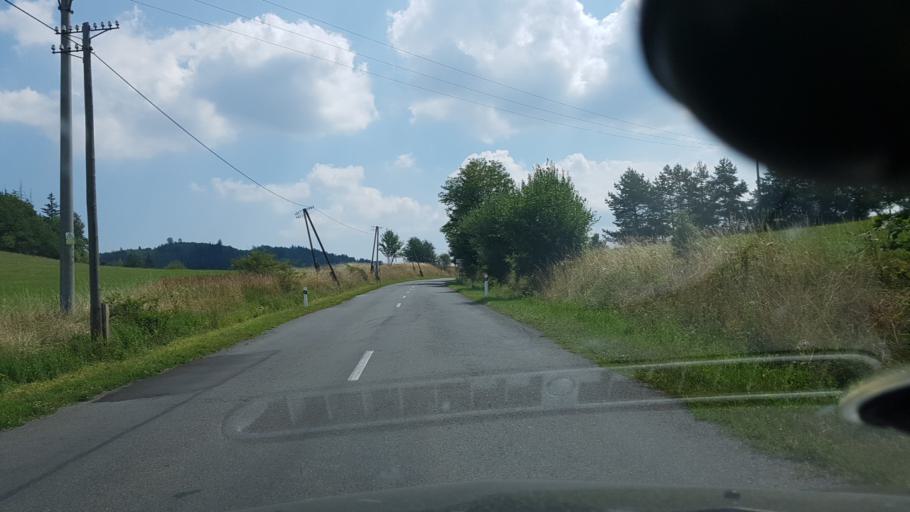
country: SK
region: Banskobystricky
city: Detva
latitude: 48.4928
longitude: 19.3464
